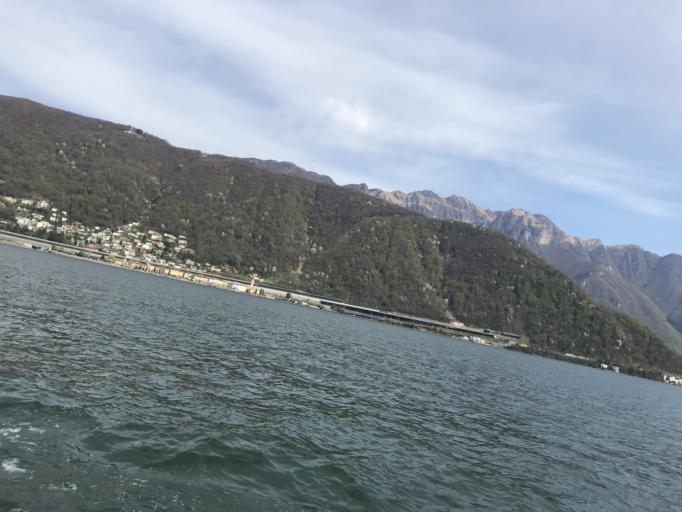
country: CH
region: Ticino
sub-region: Lugano District
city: Melide
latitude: 45.9495
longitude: 8.9505
